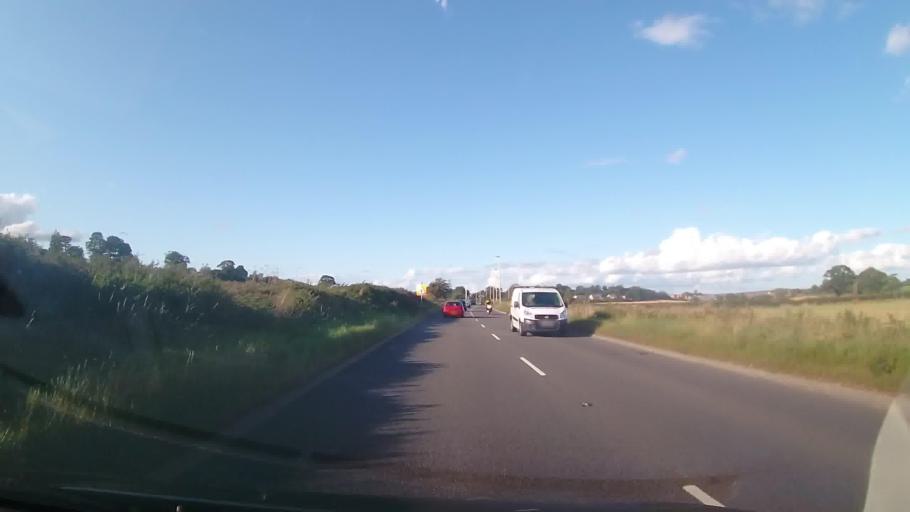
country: GB
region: England
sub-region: Shropshire
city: Bayston Hill
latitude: 52.6660
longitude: -2.7624
